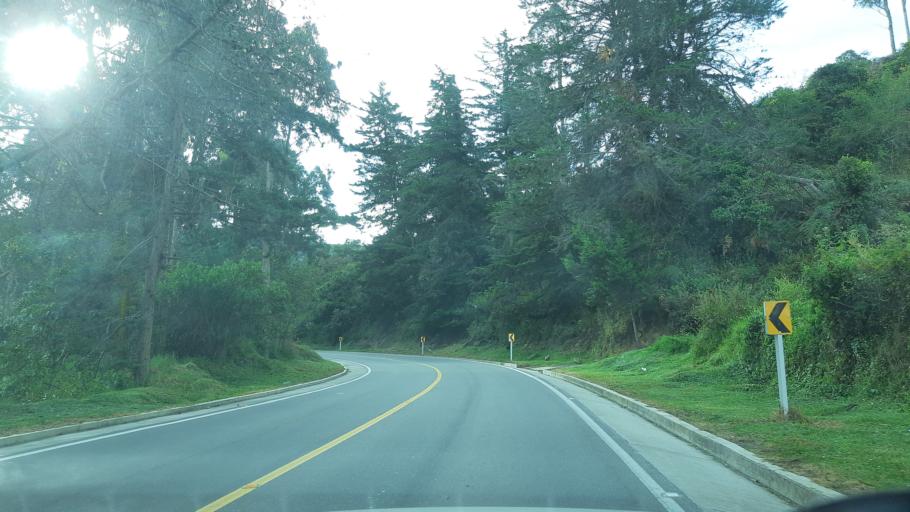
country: CO
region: Cundinamarca
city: Macheta
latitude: 5.0832
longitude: -73.6251
